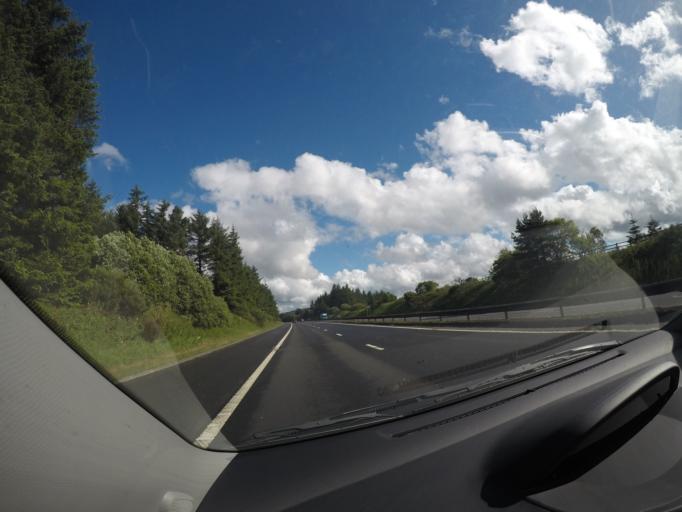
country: GB
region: Scotland
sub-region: South Lanarkshire
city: Douglas
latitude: 55.5896
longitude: -3.8296
